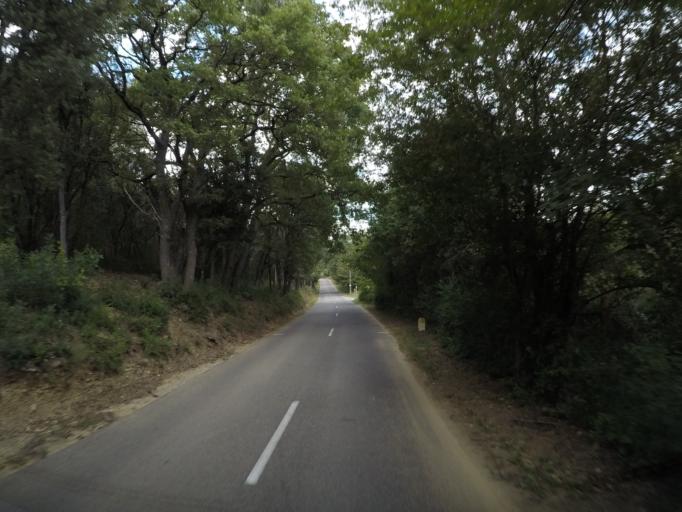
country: FR
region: Provence-Alpes-Cote d'Azur
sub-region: Departement des Alpes-de-Haute-Provence
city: Greoux-les-Bains
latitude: 43.7844
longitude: 5.9132
